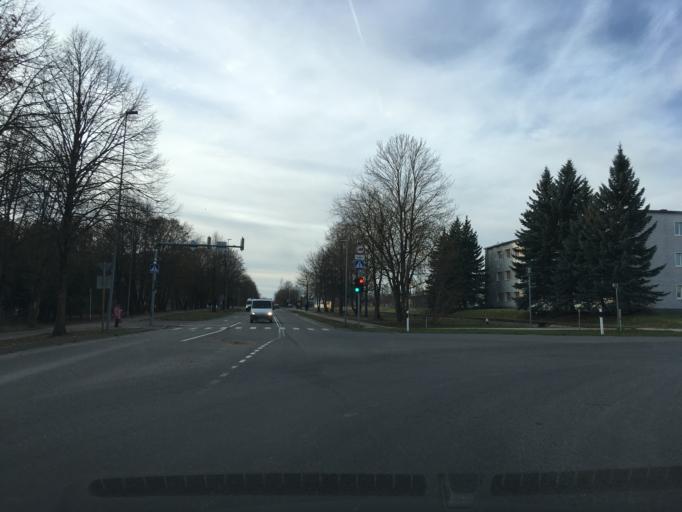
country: EE
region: Ida-Virumaa
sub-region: Johvi vald
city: Johvi
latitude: 59.3522
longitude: 27.4140
